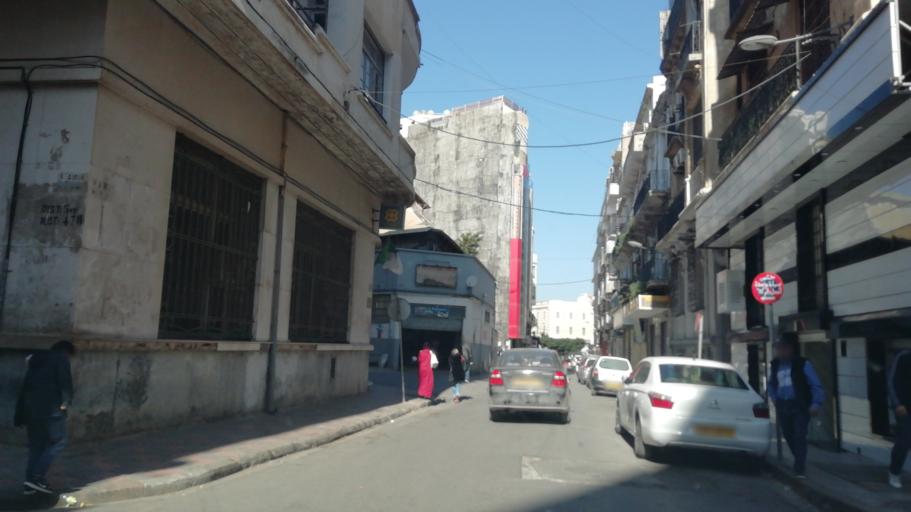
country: DZ
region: Oran
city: Oran
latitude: 35.7031
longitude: -0.6459
